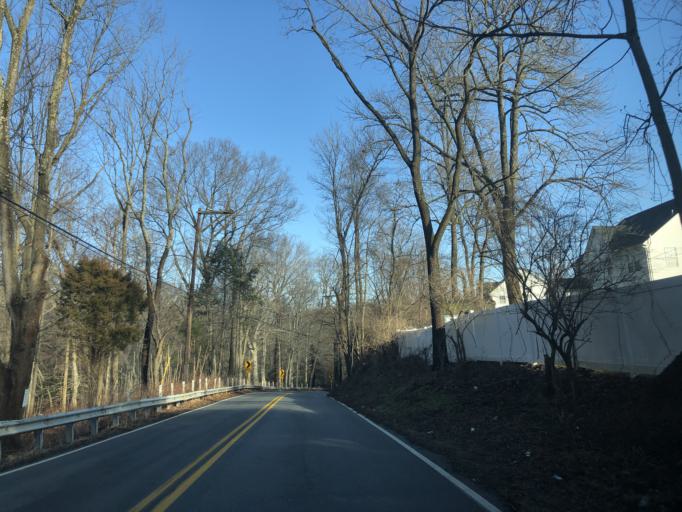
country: US
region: Pennsylvania
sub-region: Delaware County
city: Chester Heights
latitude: 39.8732
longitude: -75.4679
